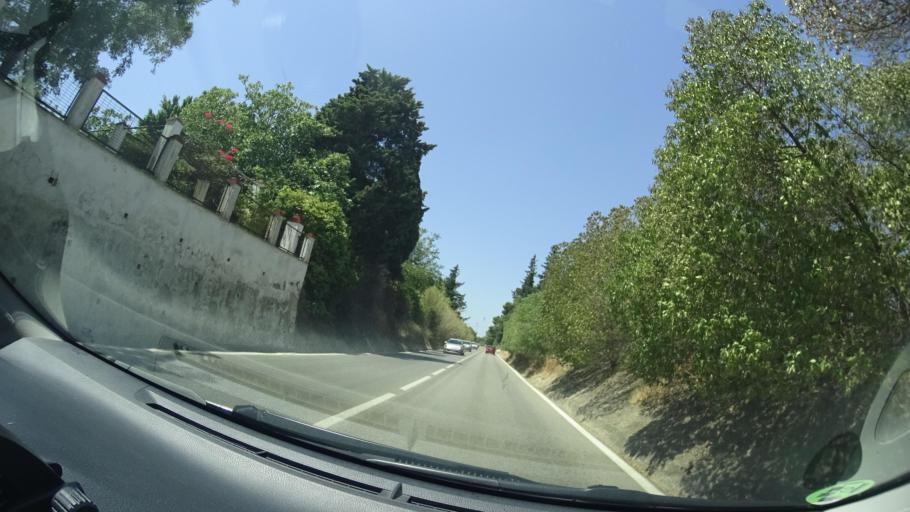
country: ES
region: Andalusia
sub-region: Provincia de Cadiz
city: Jerez de la Frontera
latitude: 36.6644
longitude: -6.1115
